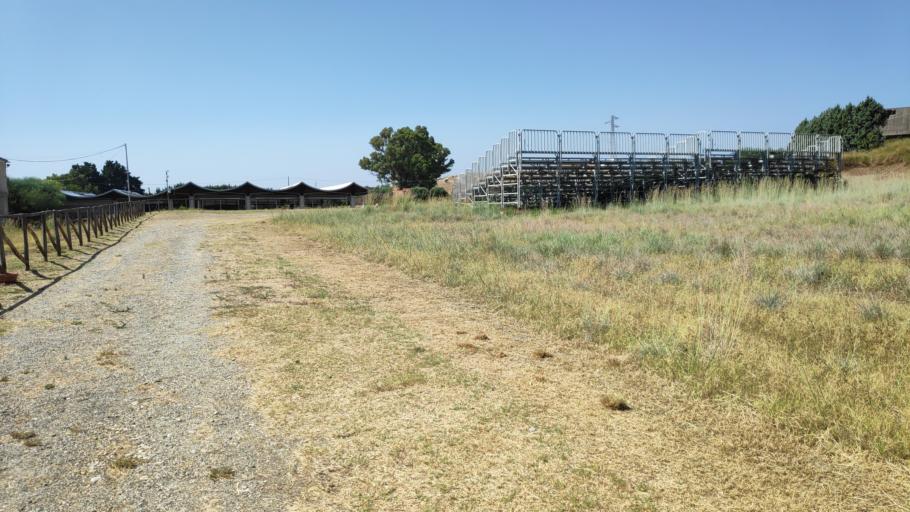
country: IT
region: Calabria
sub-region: Provincia di Reggio Calabria
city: Bianco
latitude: 38.1185
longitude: 16.1581
